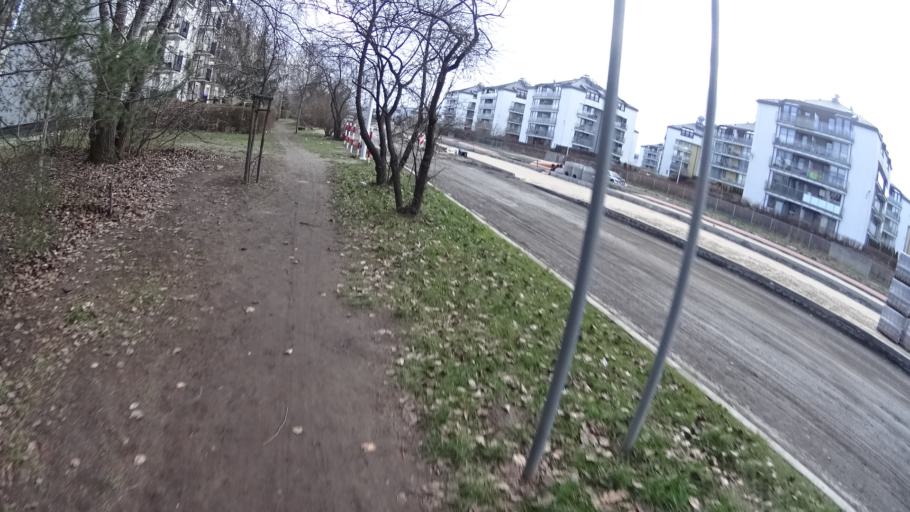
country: PL
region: Masovian Voivodeship
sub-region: Powiat pruszkowski
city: Pruszkow
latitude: 52.1606
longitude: 20.7816
